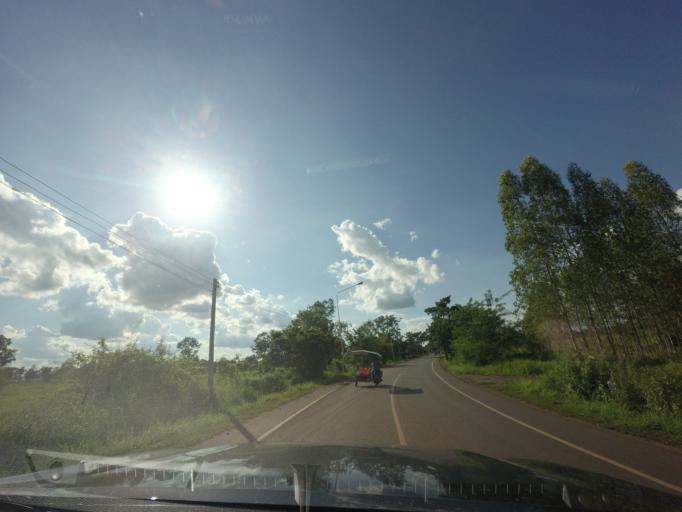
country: TH
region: Changwat Udon Thani
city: Ban Dung
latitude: 17.7389
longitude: 103.3466
